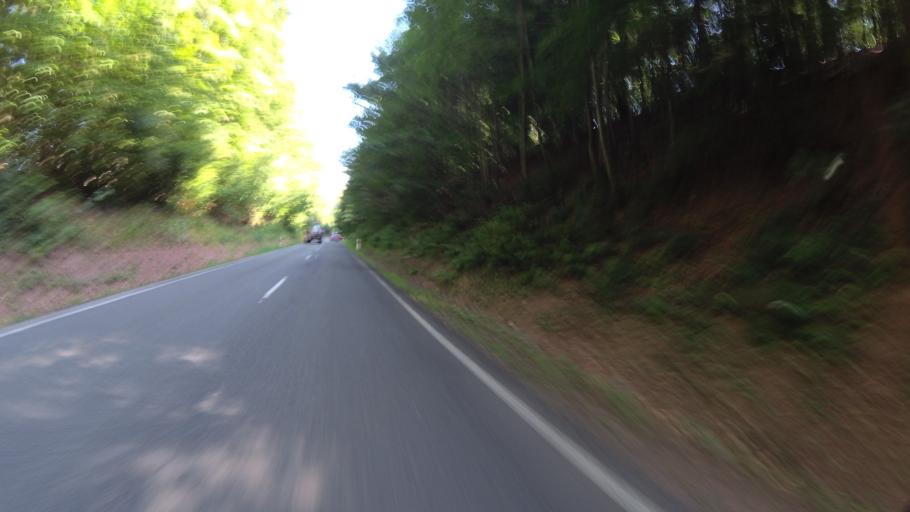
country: DE
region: Rheinland-Pfalz
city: Althornbach
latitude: 49.2149
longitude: 7.3329
